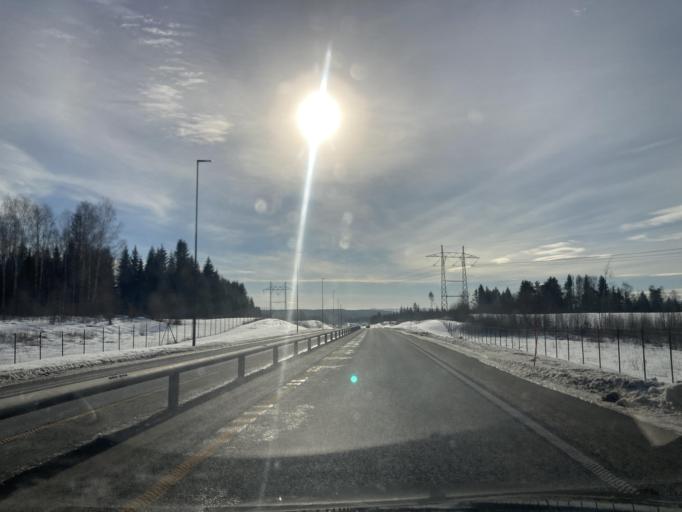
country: NO
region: Hedmark
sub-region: Loten
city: Loten
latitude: 60.8110
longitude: 11.2864
